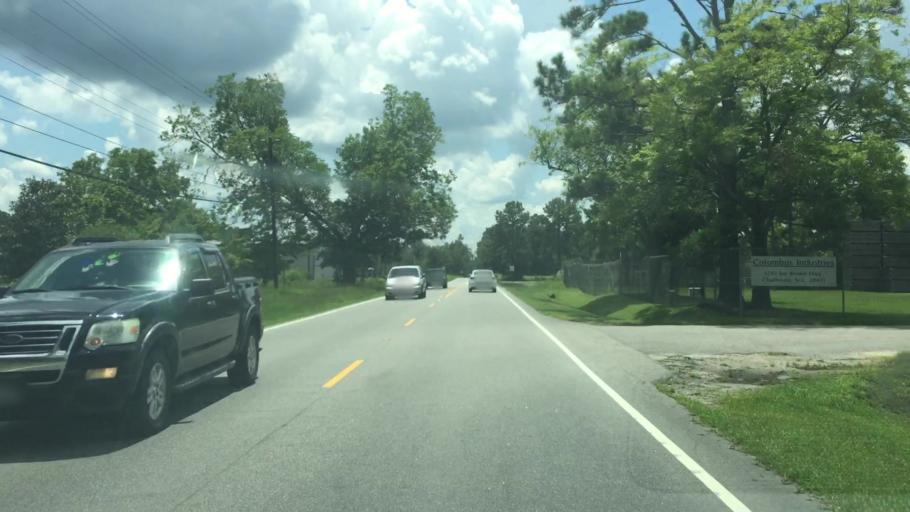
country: US
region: North Carolina
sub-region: Columbus County
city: Chadbourn
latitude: 34.3061
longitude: -78.8265
